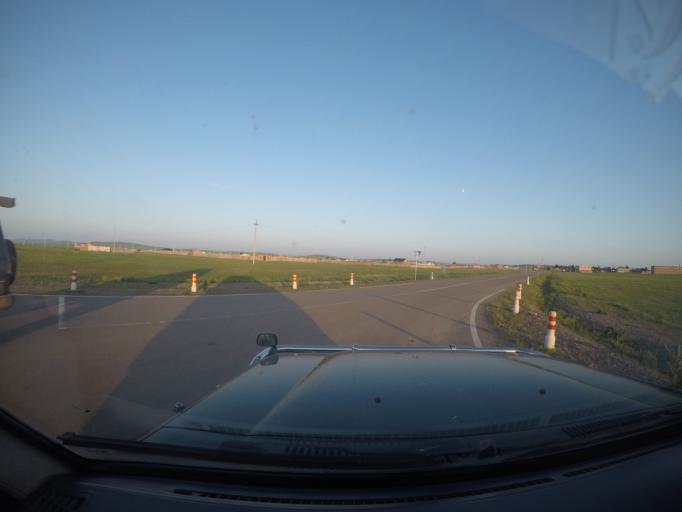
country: MN
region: Suhbaatar
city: Hanhohiy
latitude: 47.5809
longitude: 112.3489
